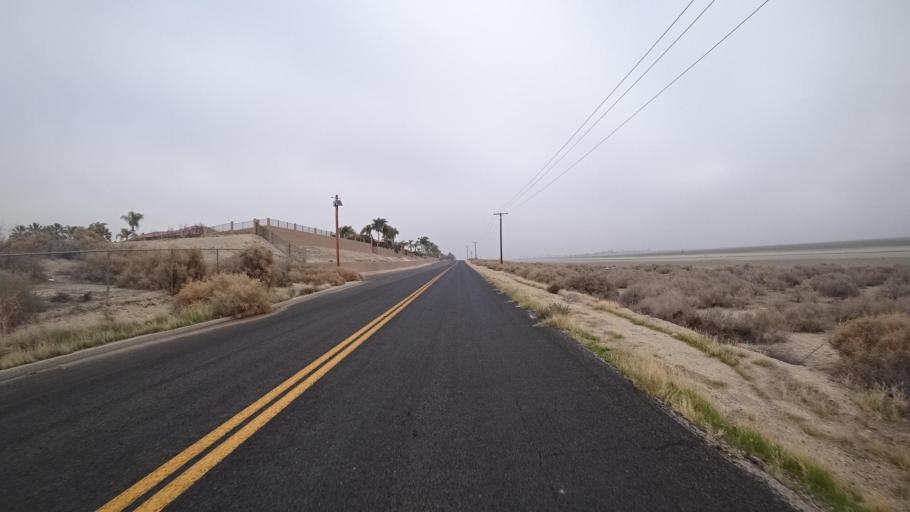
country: US
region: California
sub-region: Kern County
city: Ford City
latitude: 35.2360
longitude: -119.3239
